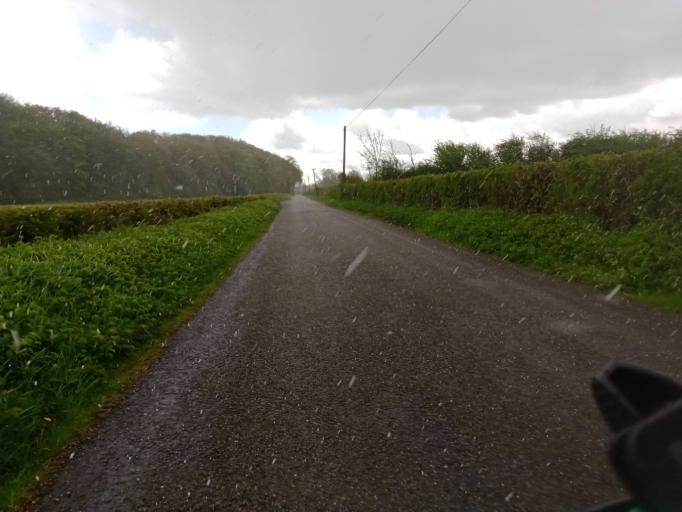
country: IE
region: Leinster
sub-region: Kilkenny
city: Kilkenny
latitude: 52.6894
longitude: -7.2709
